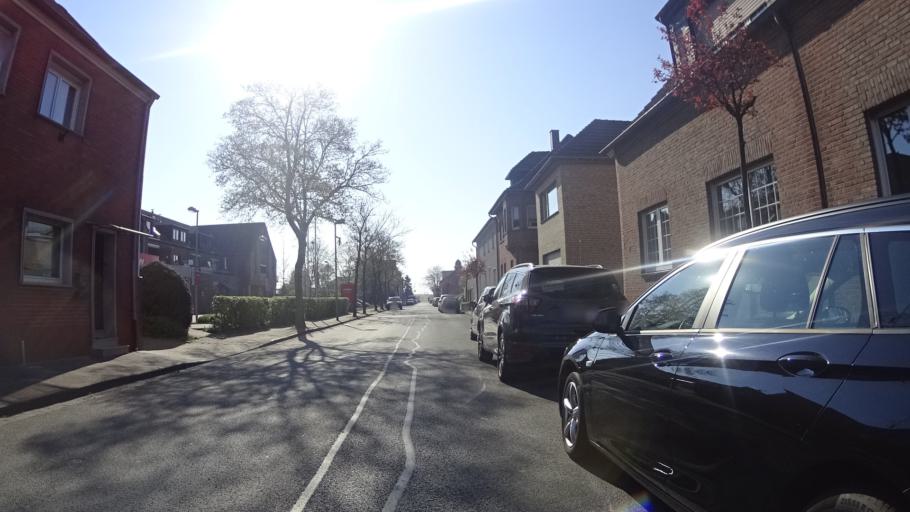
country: DE
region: North Rhine-Westphalia
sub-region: Regierungsbezirk Dusseldorf
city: Wesel
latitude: 51.6287
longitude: 6.5823
